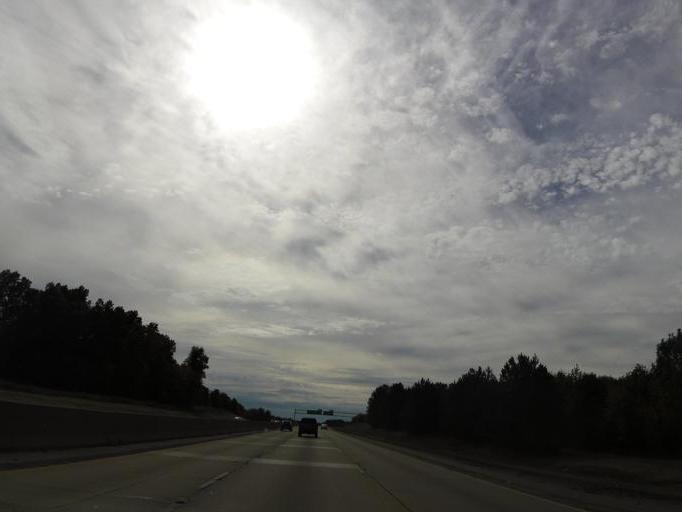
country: US
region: Ohio
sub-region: Summit County
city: Hudson
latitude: 41.2092
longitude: -81.4862
